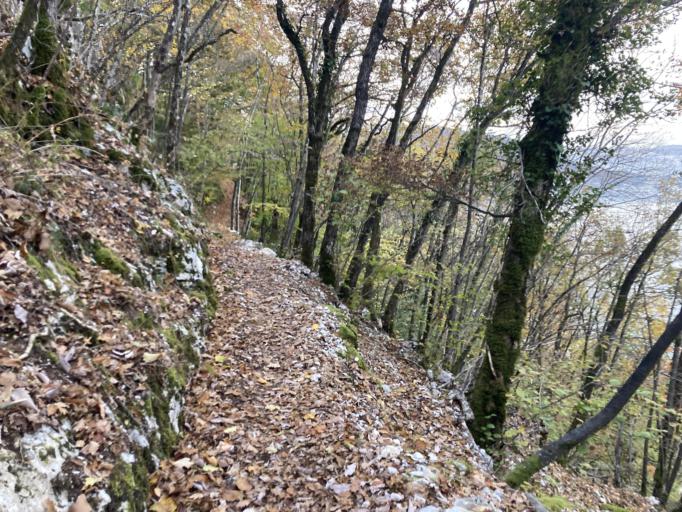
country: FR
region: Rhone-Alpes
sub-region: Departement de la Haute-Savoie
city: Annecy-le-Vieux
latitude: 45.9081
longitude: 6.1678
